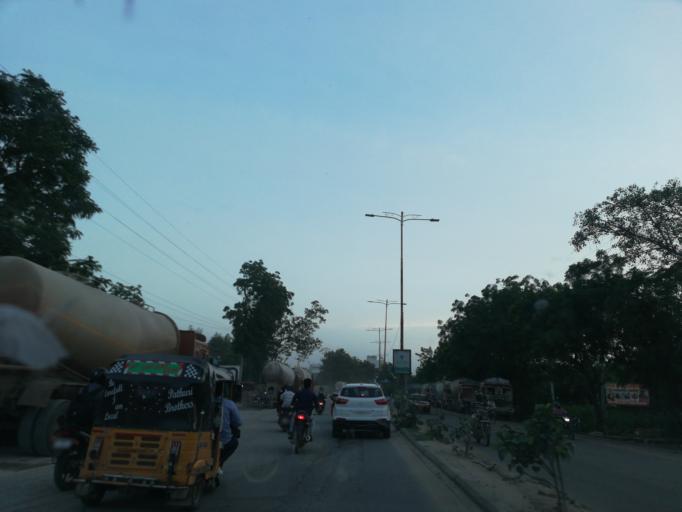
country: IN
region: Telangana
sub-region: Medak
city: Serilingampalle
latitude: 17.5310
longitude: 78.3560
